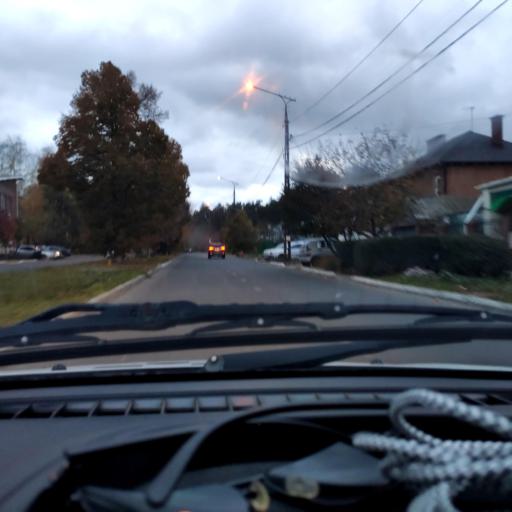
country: RU
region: Samara
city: Tol'yatti
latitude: 53.5150
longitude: 49.3974
